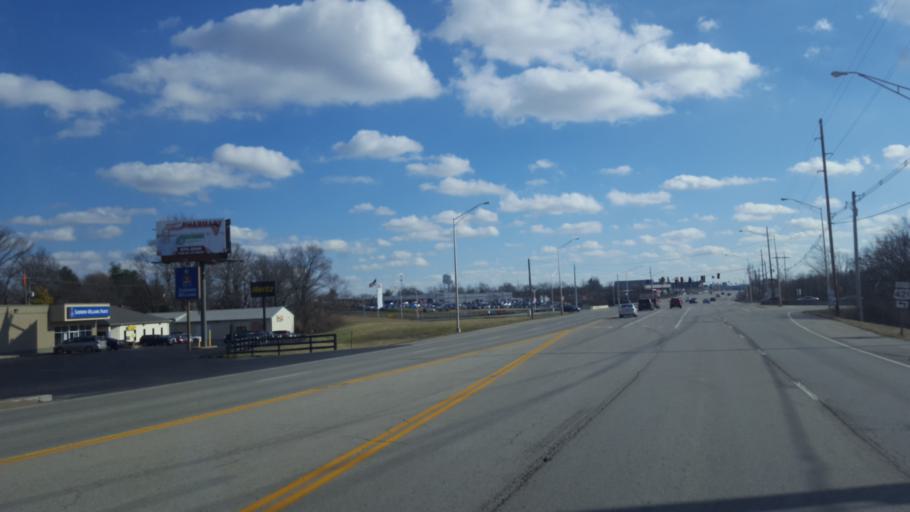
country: US
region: Kentucky
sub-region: Franklin County
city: Frankfort
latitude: 38.1901
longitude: -84.8230
